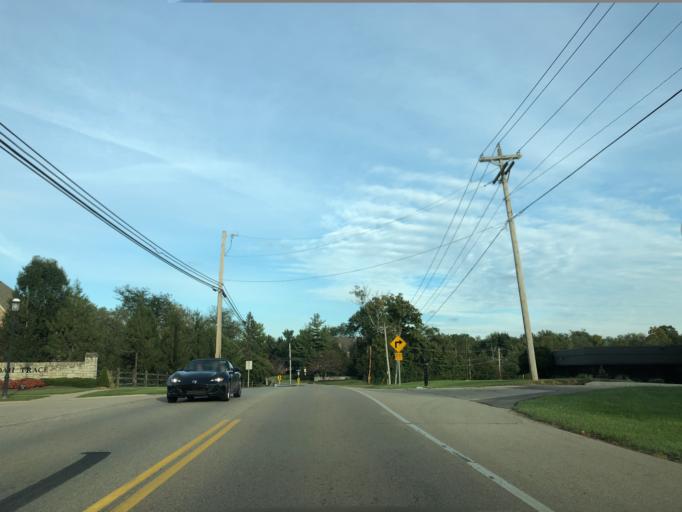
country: US
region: Ohio
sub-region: Hamilton County
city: Sixteen Mile Stand
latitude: 39.2844
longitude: -84.2983
